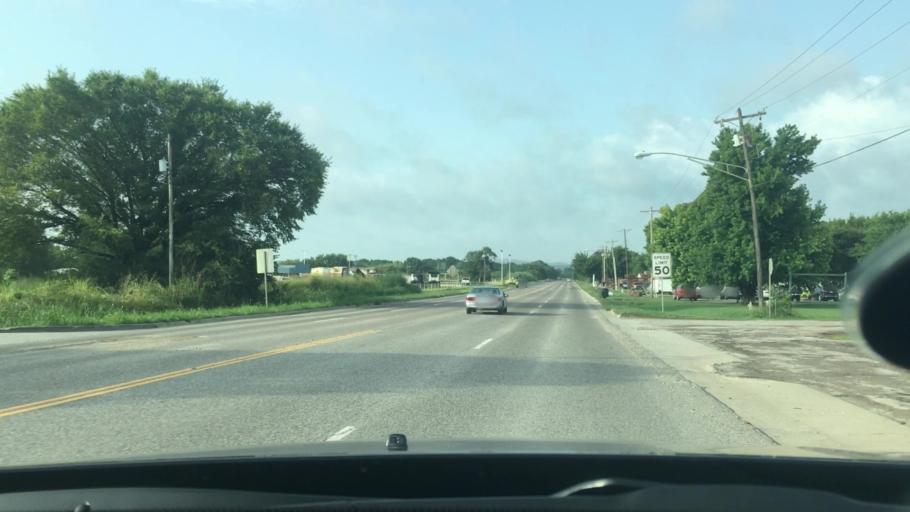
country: US
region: Oklahoma
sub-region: Murray County
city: Davis
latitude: 34.4980
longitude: -97.1259
